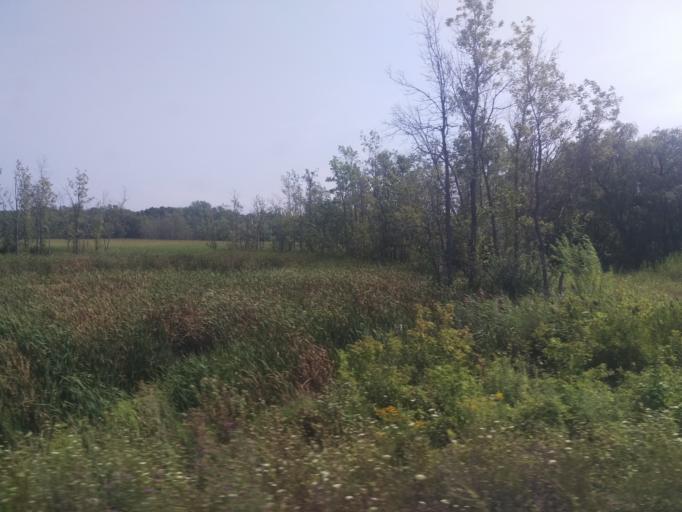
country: CA
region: Ontario
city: Kingston
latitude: 44.2604
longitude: -76.5306
